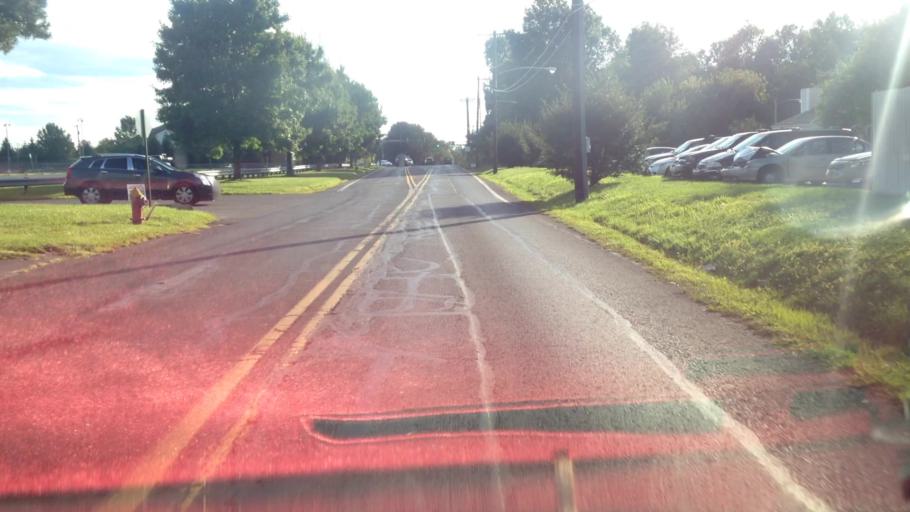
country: US
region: Pennsylvania
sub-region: Bucks County
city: Penndel
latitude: 40.1331
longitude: -74.9408
